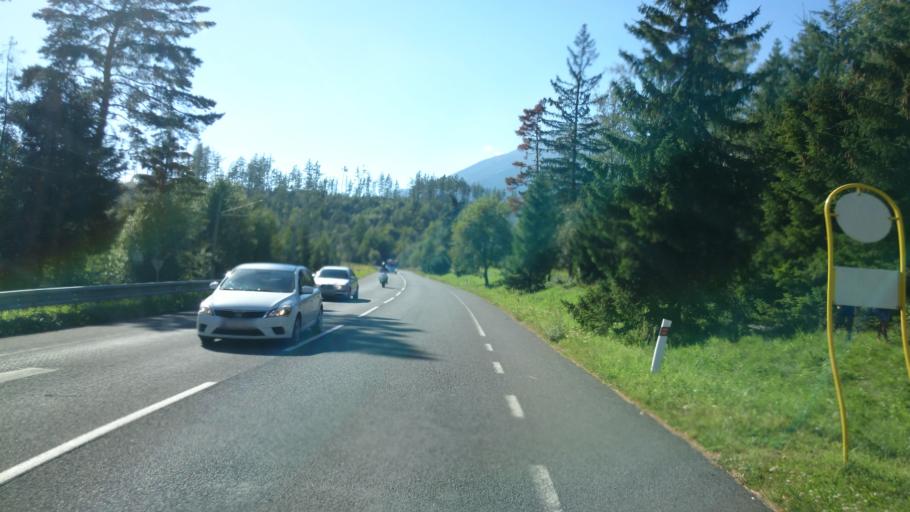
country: SK
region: Presovsky
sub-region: Okres Poprad
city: Vysoke Tatry
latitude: 49.1501
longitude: 20.2575
